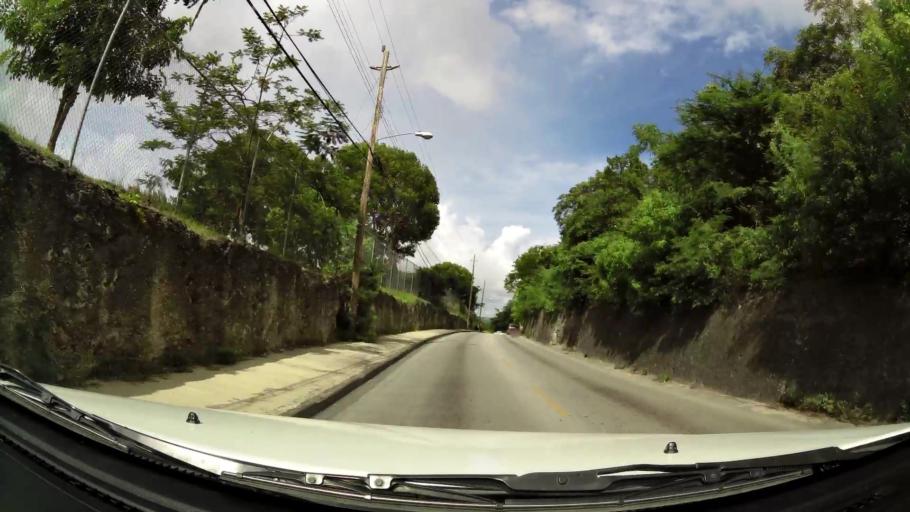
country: BB
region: Saint Michael
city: Bridgetown
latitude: 13.1166
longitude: -59.6010
